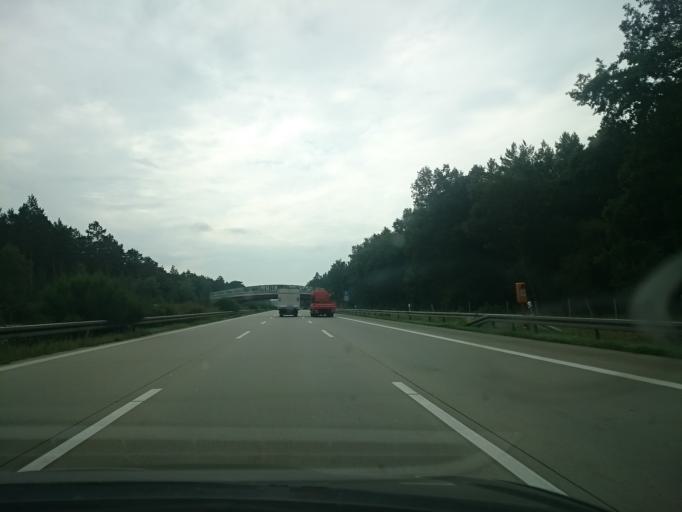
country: DE
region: Brandenburg
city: Niemegk
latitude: 52.0696
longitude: 12.6580
